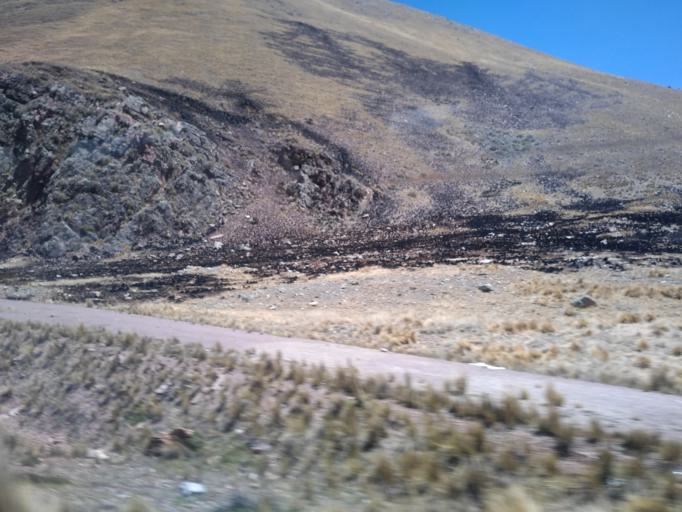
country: PE
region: Cusco
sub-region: Provincia de Canas
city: Layo
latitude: -14.4806
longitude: -71.0068
